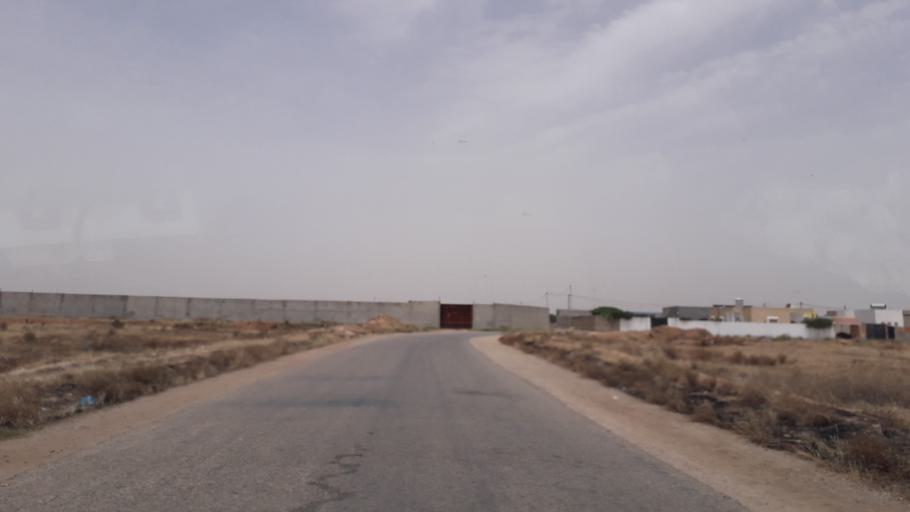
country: TN
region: Safaqis
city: Al Qarmadah
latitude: 34.8463
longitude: 10.7553
